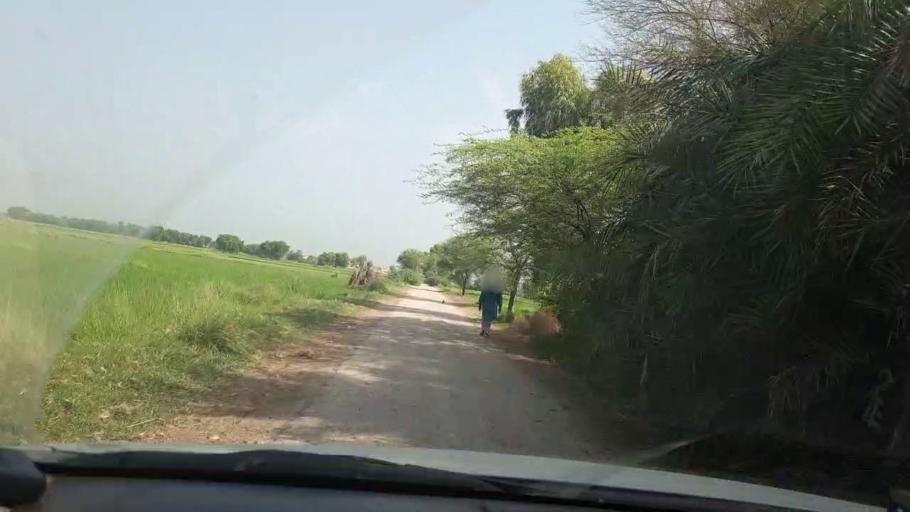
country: PK
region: Sindh
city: Chak
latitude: 27.8308
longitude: 68.7997
